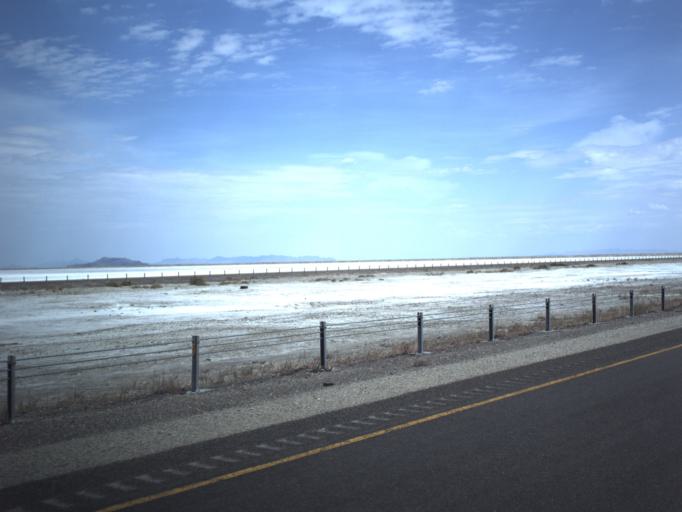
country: US
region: Utah
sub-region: Tooele County
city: Wendover
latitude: 40.7381
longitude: -113.8331
